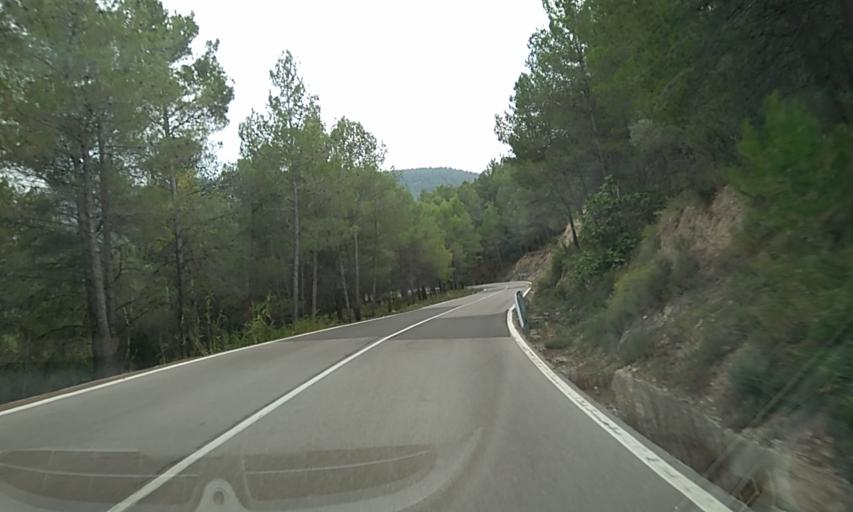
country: ES
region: Valencia
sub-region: Provincia de Castello
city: Puebla de Arenoso
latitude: 40.0933
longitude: -0.5672
